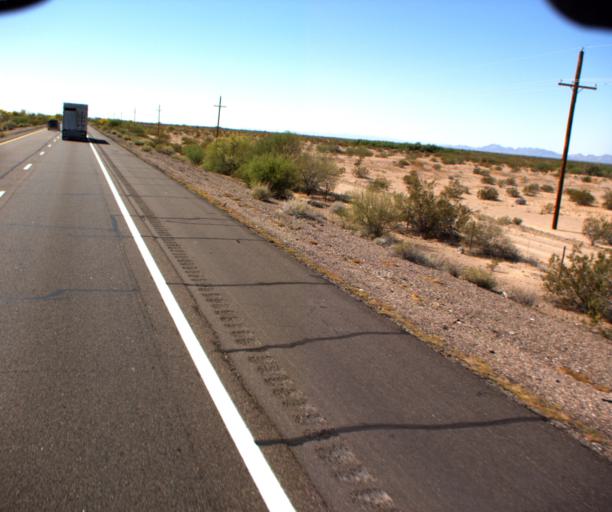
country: US
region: Arizona
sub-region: Maricopa County
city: Gila Bend
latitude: 32.8420
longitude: -113.3095
